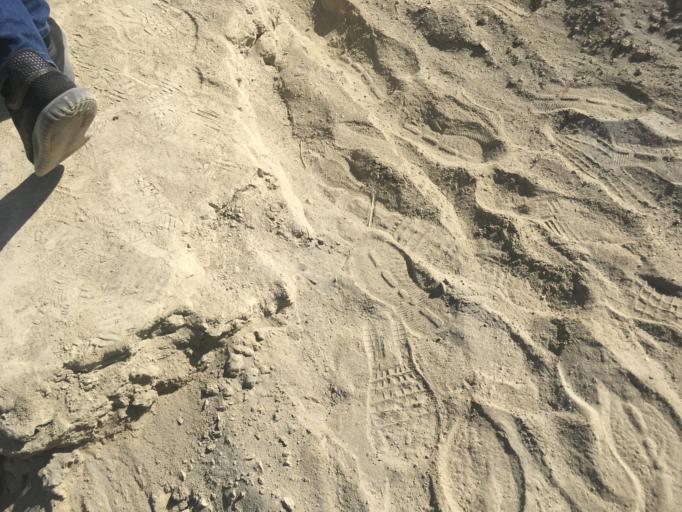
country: PK
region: Gilgit-Baltistan
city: Skardu
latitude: 35.3313
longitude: 75.5220
